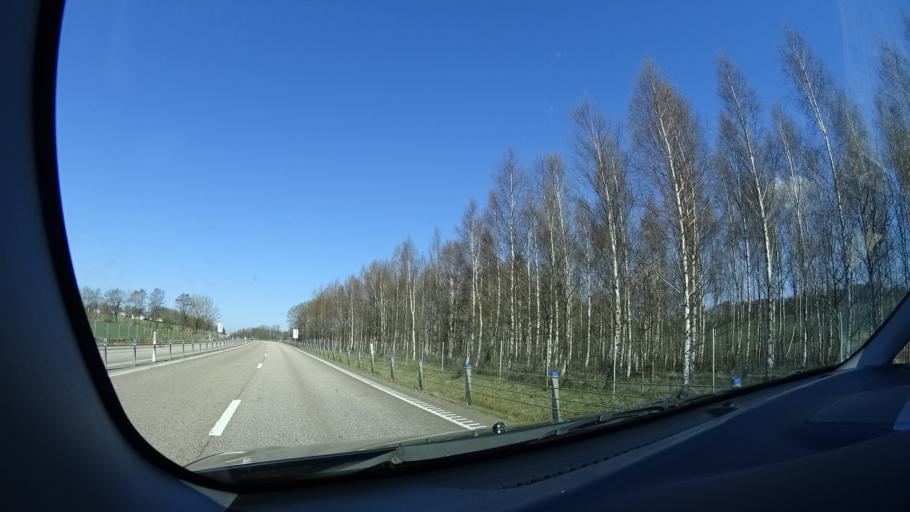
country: SE
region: Skane
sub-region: Astorps Kommun
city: Astorp
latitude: 56.1801
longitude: 12.9008
